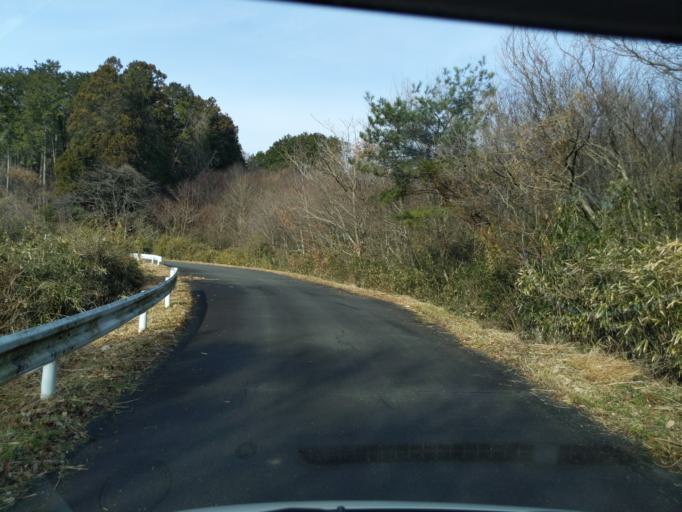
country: JP
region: Miyagi
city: Wakuya
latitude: 38.7017
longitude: 141.1560
